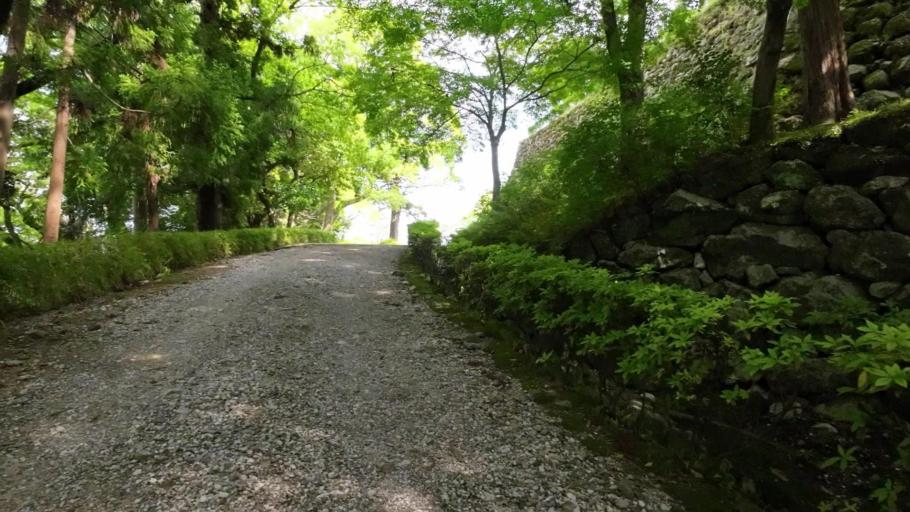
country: JP
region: Kochi
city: Kochi-shi
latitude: 33.5622
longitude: 133.5318
